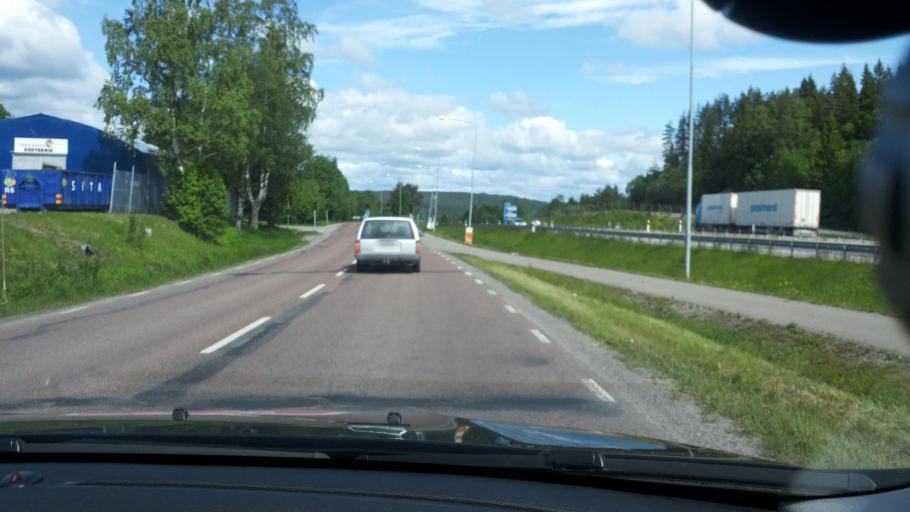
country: SE
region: Vaesternorrland
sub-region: Sundsvalls Kommun
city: Johannedal
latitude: 62.4293
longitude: 17.3461
